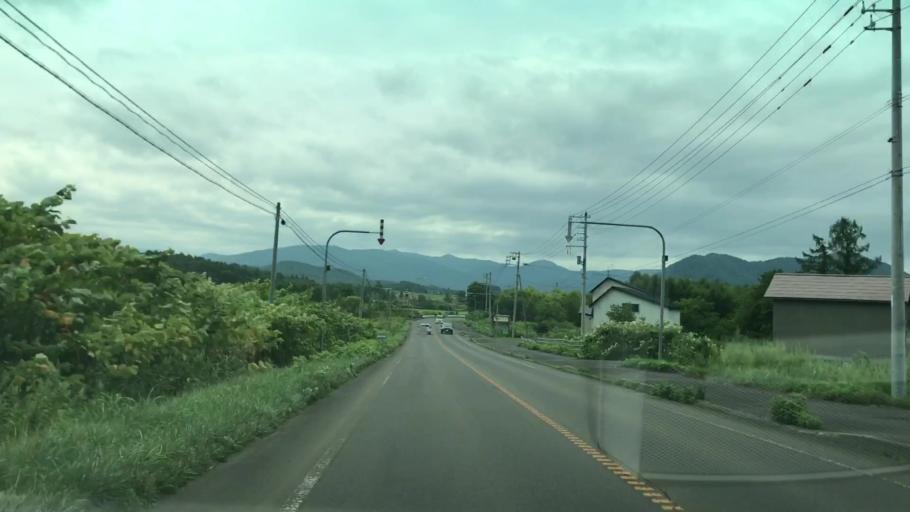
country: JP
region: Hokkaido
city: Yoichi
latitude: 43.1018
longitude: 140.8237
